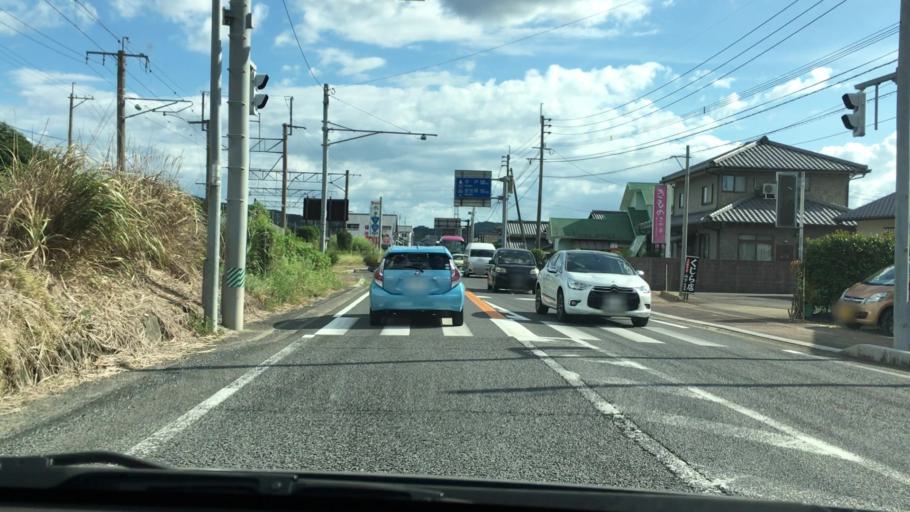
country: JP
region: Saga Prefecture
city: Imaricho-ko
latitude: 33.1848
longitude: 129.8545
